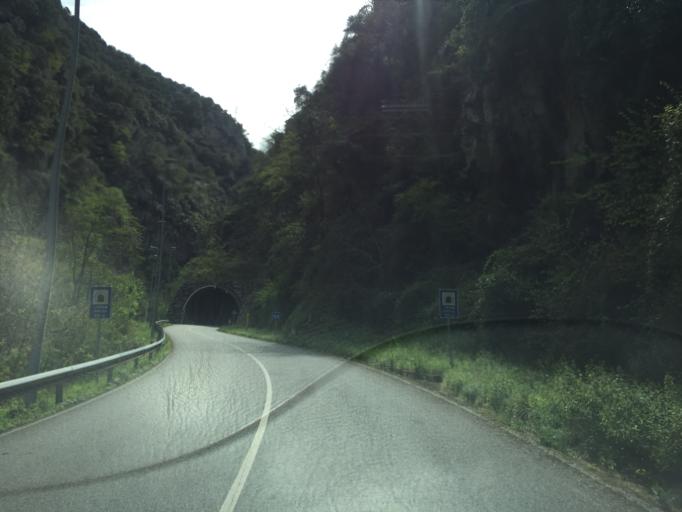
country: ES
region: Asturias
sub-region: Province of Asturias
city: Proaza
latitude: 43.2337
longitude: -6.0328
